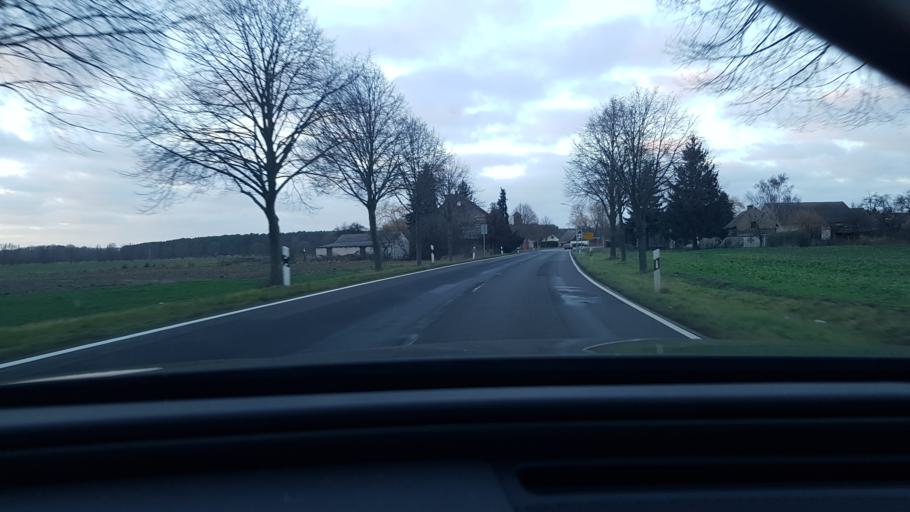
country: DE
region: Brandenburg
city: Storkow
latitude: 52.2796
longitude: 13.9053
